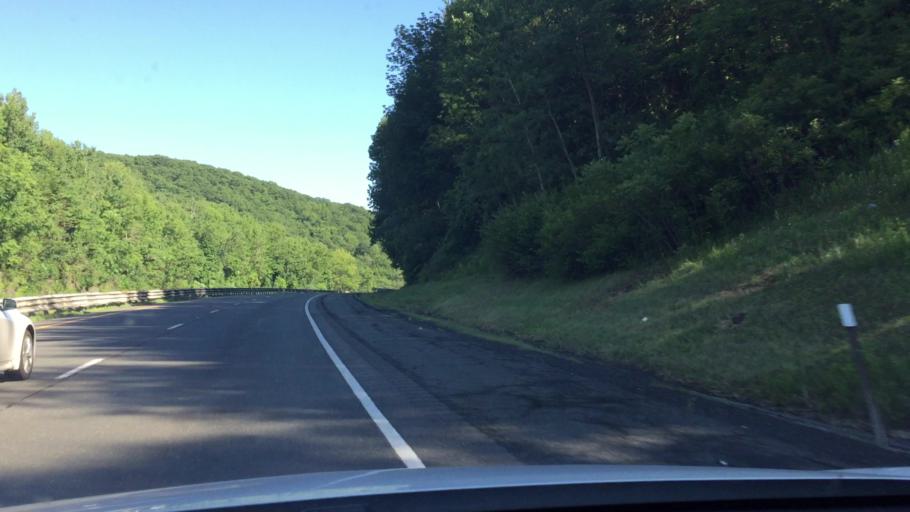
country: US
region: Massachusetts
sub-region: Berkshire County
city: West Stockbridge
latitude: 42.3099
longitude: -73.3559
